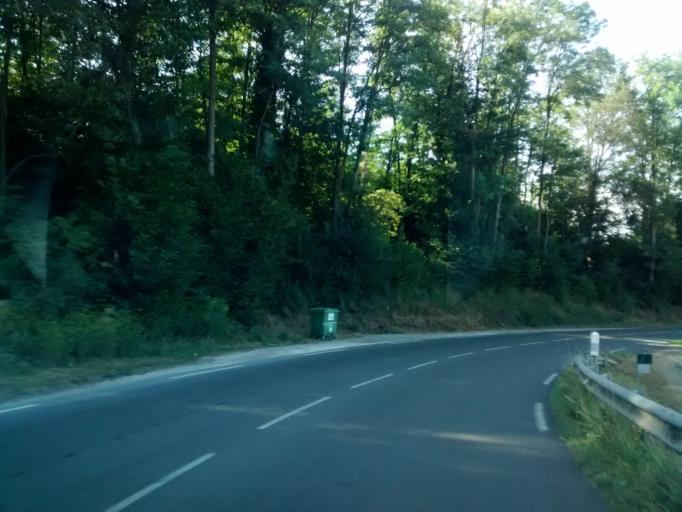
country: FR
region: Aquitaine
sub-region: Departement de la Dordogne
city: Sarlat-la-Caneda
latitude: 44.9200
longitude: 1.2061
